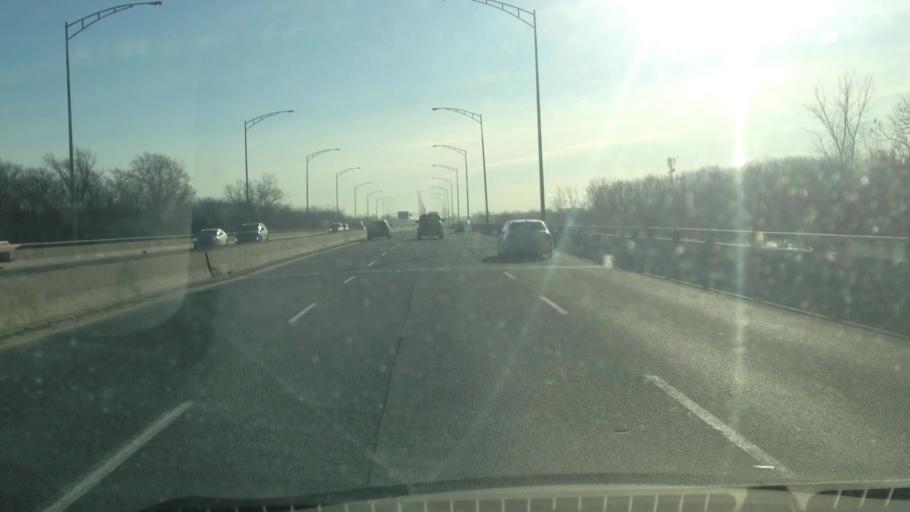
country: CA
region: Quebec
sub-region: Laurentides
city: Boisbriand
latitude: 45.5817
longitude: -73.8387
